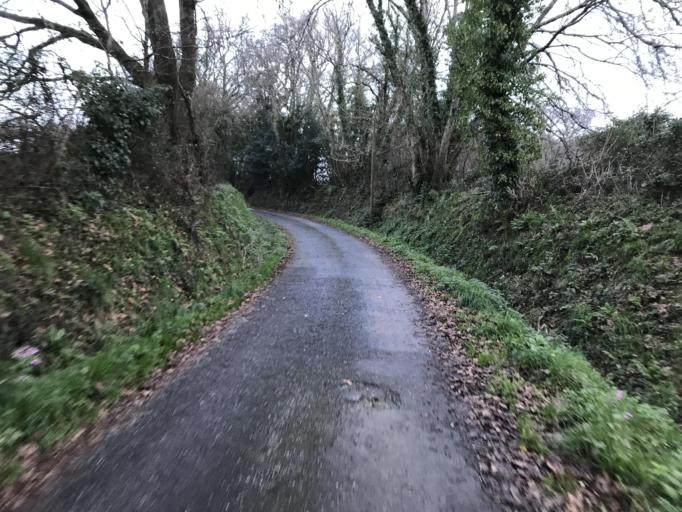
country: FR
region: Brittany
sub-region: Departement du Finistere
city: Loperhet
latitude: 48.3633
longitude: -4.3173
